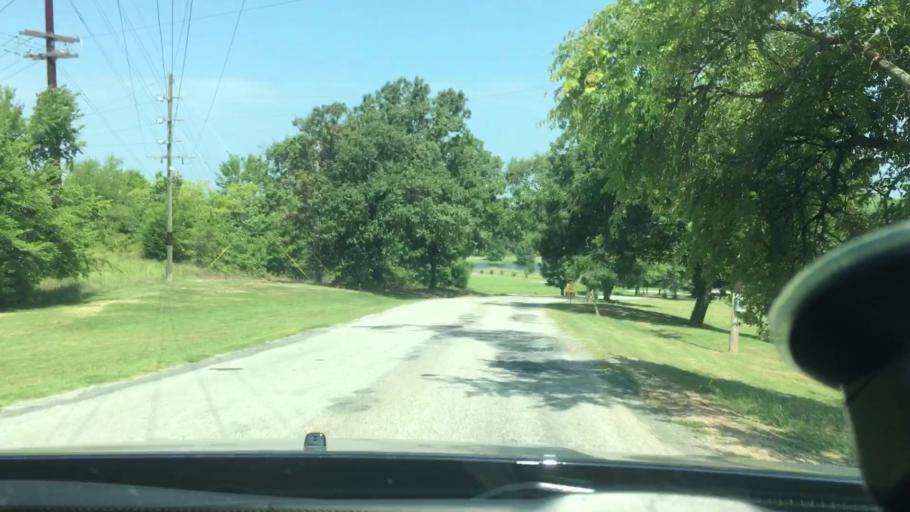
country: US
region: Oklahoma
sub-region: Pontotoc County
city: Ada
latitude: 34.7815
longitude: -96.5998
